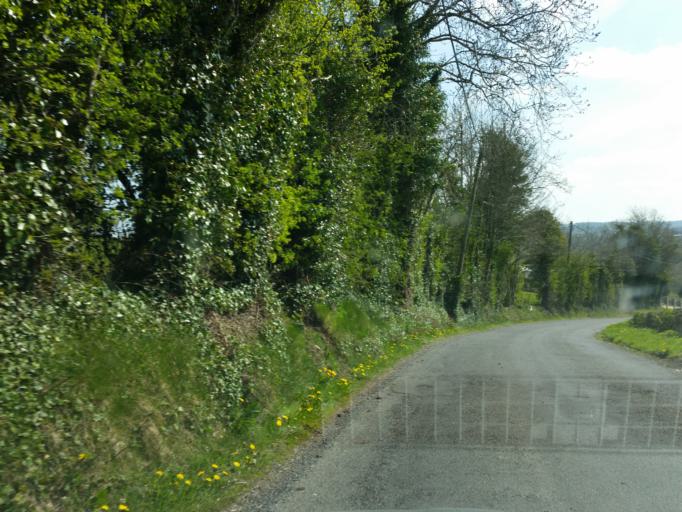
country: GB
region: Northern Ireland
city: Lisnaskea
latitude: 54.3179
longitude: -7.3903
